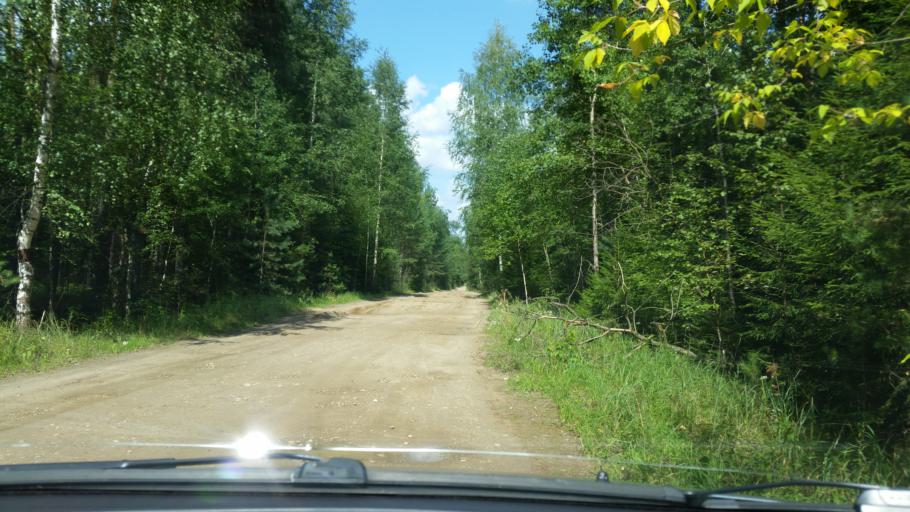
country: RU
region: Moskovskaya
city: Pushchino
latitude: 54.9095
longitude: 37.6857
